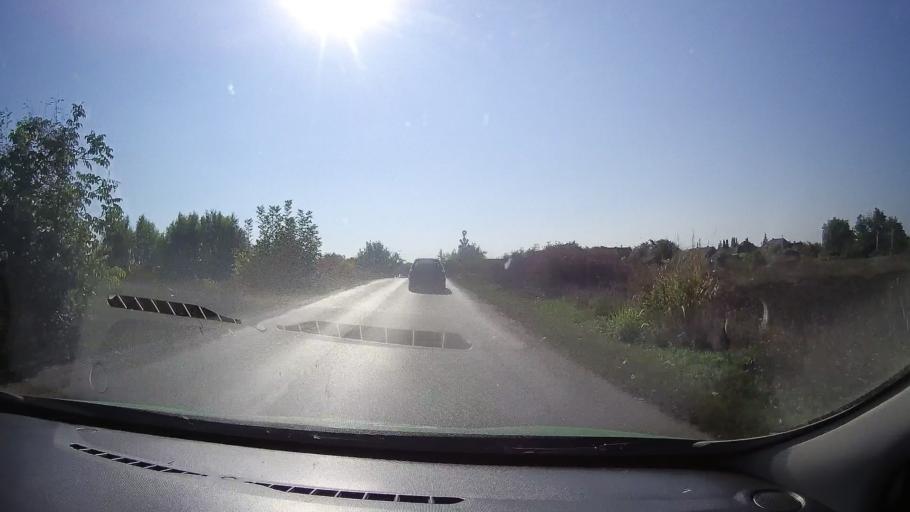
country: RO
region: Satu Mare
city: Carei
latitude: 47.6974
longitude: 22.4723
